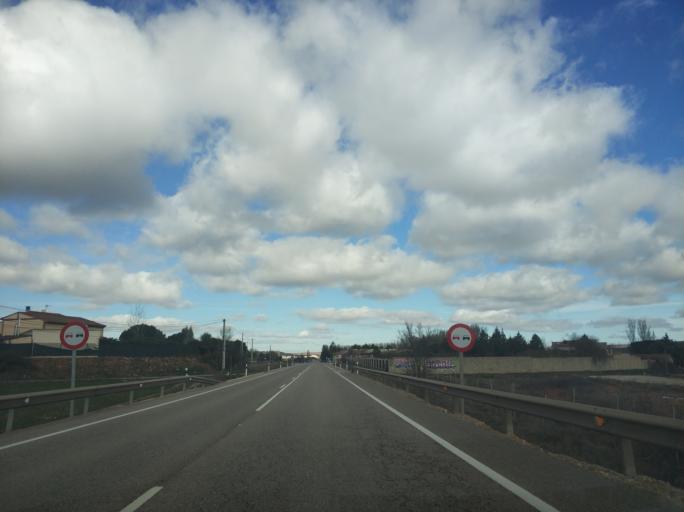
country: ES
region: Castille and Leon
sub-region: Provincia de Burgos
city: Revillarruz
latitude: 42.2277
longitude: -3.6581
